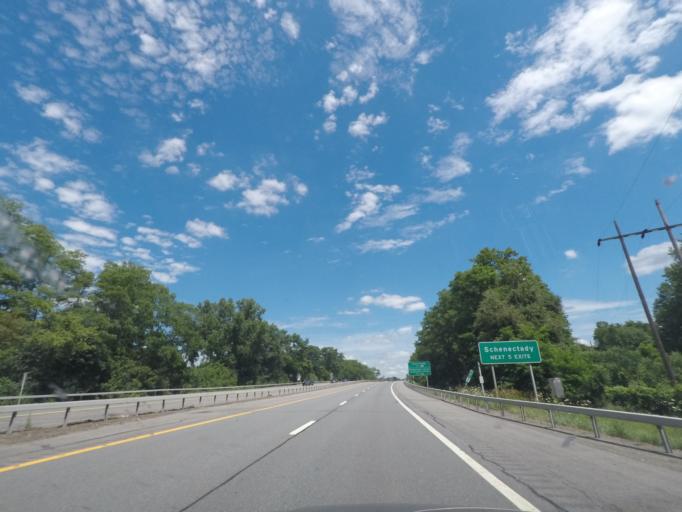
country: US
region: New York
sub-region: Schenectady County
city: Schenectady
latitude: 42.7761
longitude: -73.9254
